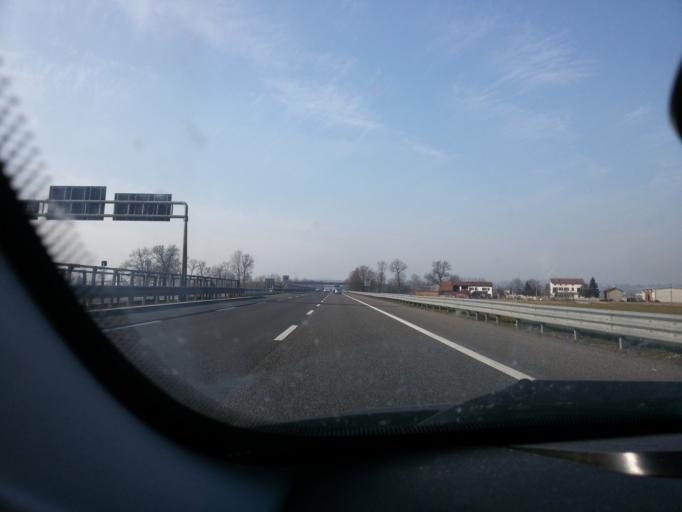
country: IT
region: Piedmont
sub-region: Provincia di Alessandria
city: Castelletto Monferrato
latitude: 44.9422
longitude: 8.5685
